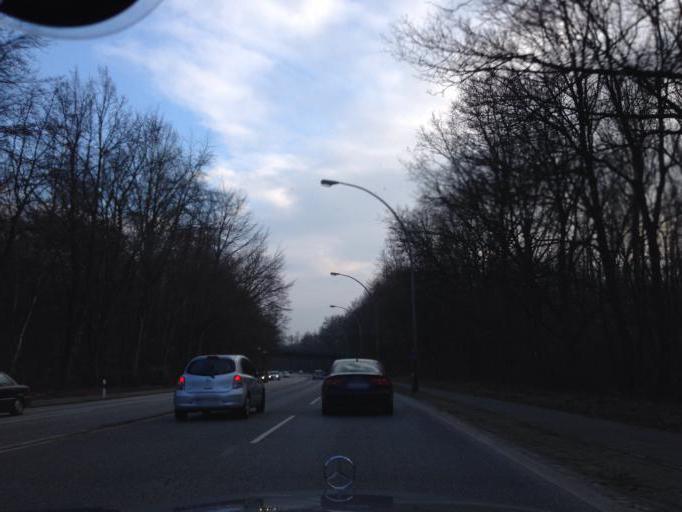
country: DE
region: Schleswig-Holstein
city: Glinde
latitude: 53.5020
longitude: 10.1855
